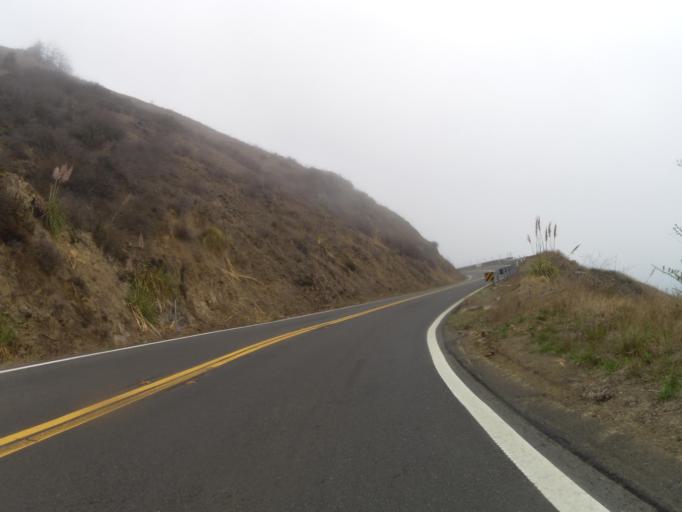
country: US
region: California
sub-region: Sonoma County
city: Monte Rio
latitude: 38.4874
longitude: -123.1862
